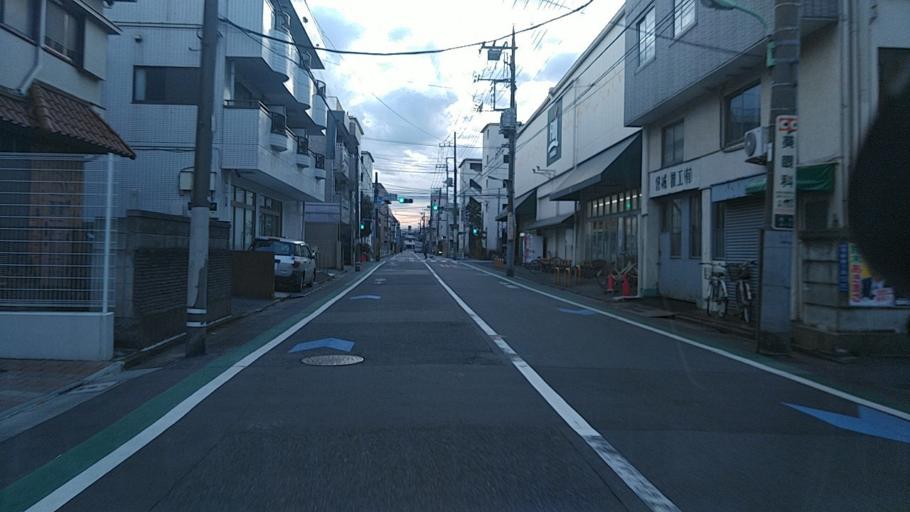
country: JP
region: Kanagawa
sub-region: Kawasaki-shi
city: Kawasaki
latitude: 35.5494
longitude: 139.7475
